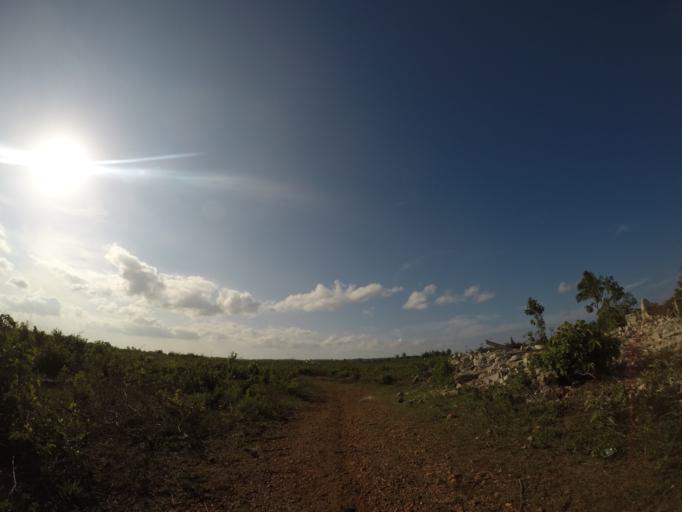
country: TZ
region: Zanzibar Central/South
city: Koani
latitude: -6.2064
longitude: 39.3150
